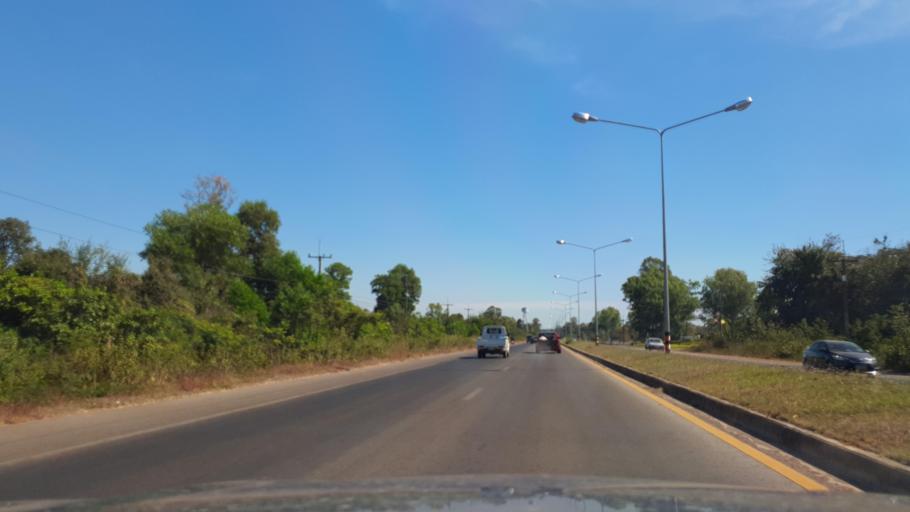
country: TH
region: Sakon Nakhon
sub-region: Amphoe Khok Si Suphan
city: Khok Si Suphan
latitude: 17.0772
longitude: 104.2017
